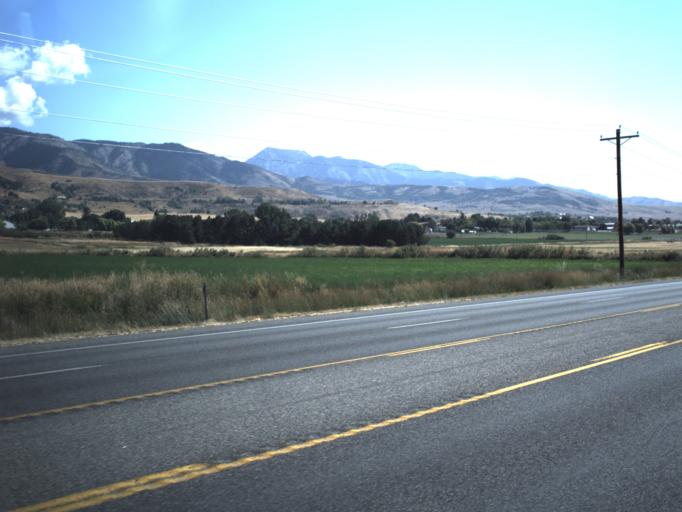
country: US
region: Utah
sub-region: Cache County
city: Richmond
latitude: 41.9337
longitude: -111.8141
